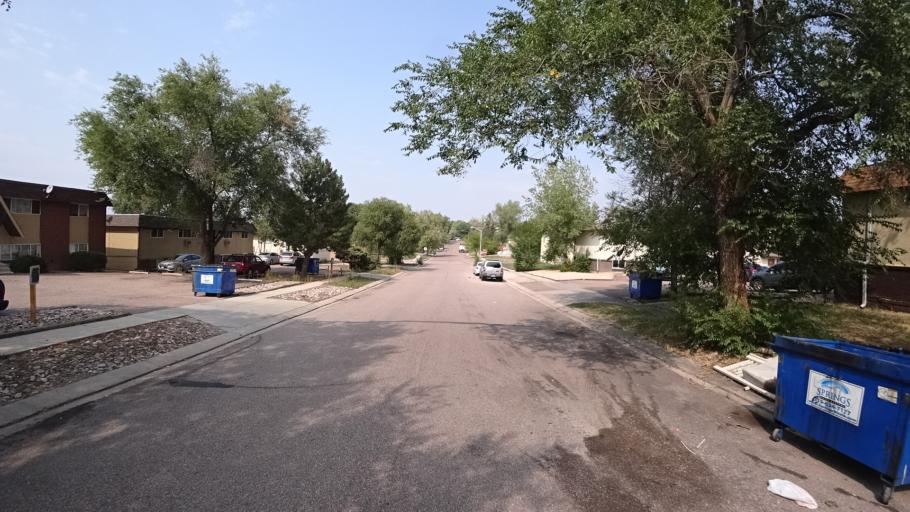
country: US
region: Colorado
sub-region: El Paso County
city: Cimarron Hills
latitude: 38.8261
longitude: -104.7476
